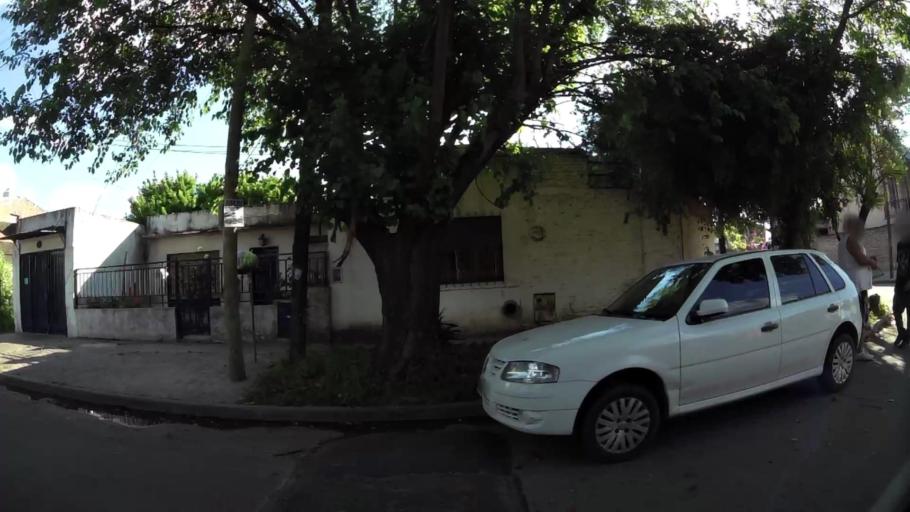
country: AR
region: Buenos Aires
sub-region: Partido de Moron
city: Moron
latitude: -34.6889
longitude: -58.6019
